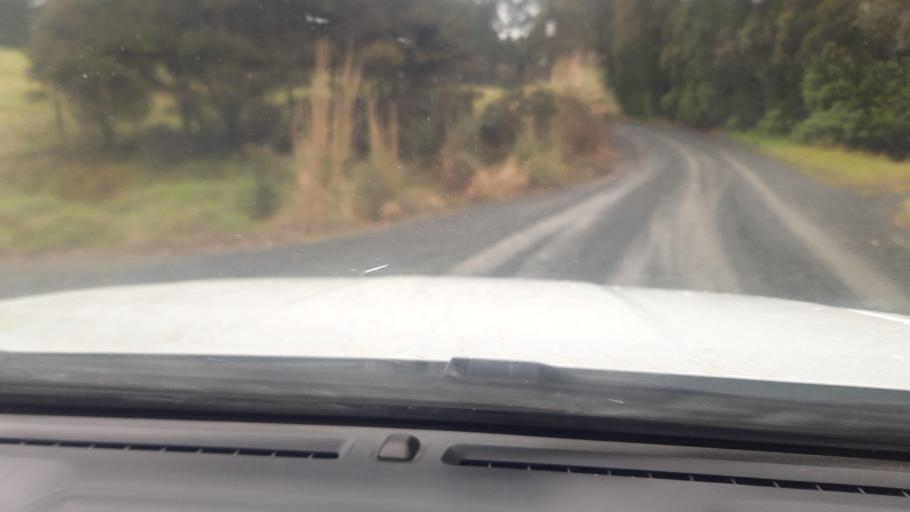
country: NZ
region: Northland
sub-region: Far North District
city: Kaitaia
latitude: -34.9801
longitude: 173.2057
